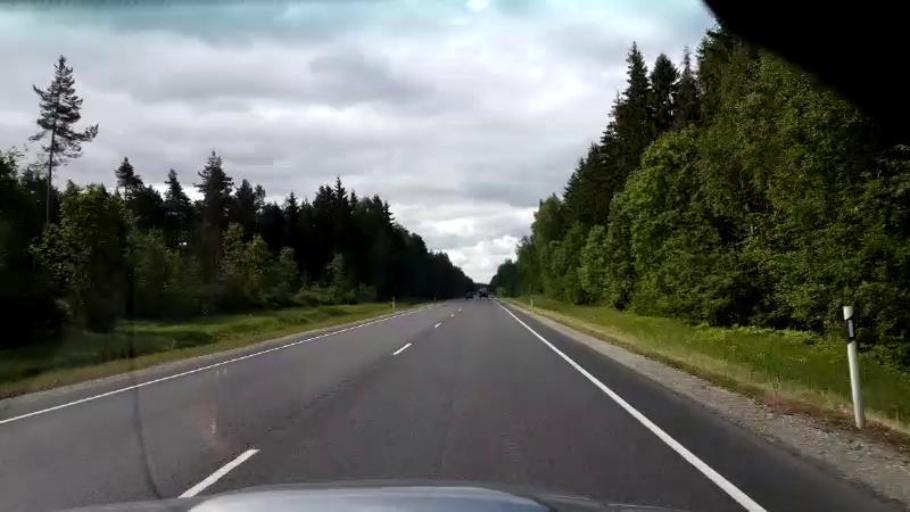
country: EE
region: Raplamaa
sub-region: Maerjamaa vald
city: Marjamaa
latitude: 58.9067
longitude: 24.4560
